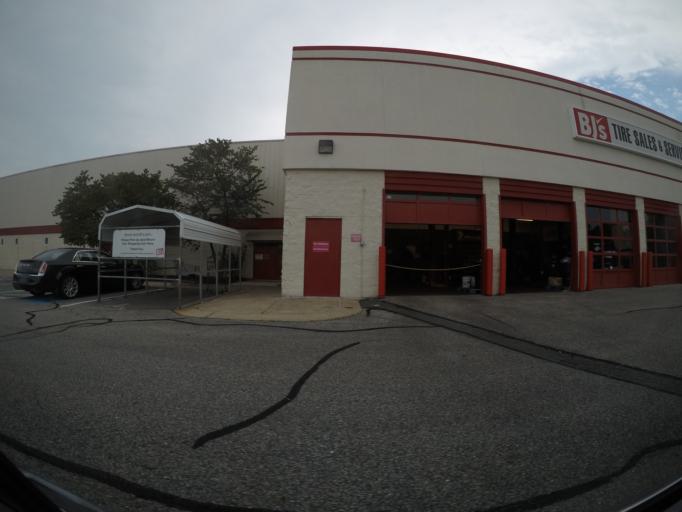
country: US
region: Maryland
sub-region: Harford County
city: Joppatowne
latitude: 39.4541
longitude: -76.3198
